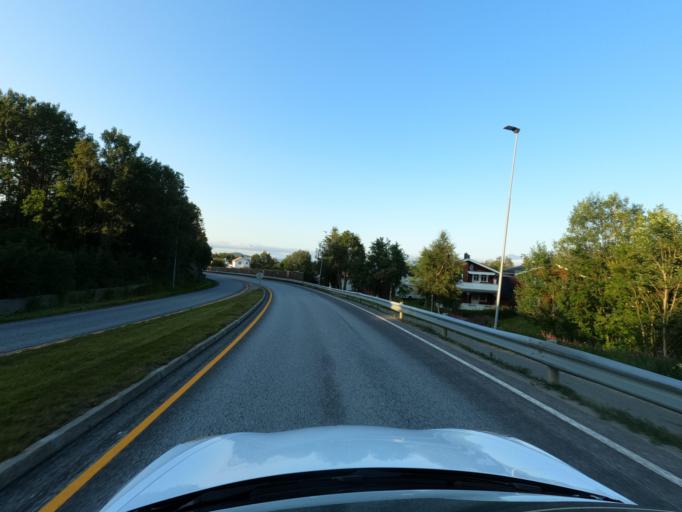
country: NO
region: Troms
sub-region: Harstad
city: Harstad
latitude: 68.7417
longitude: 16.5667
